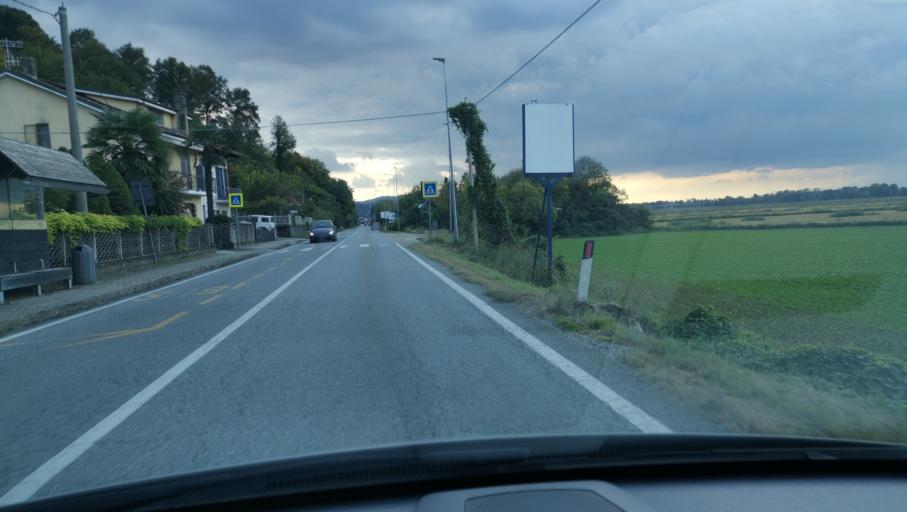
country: IT
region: Piedmont
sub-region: Provincia di Torino
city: Piana San Raffaele
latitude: 45.1648
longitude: 7.8571
